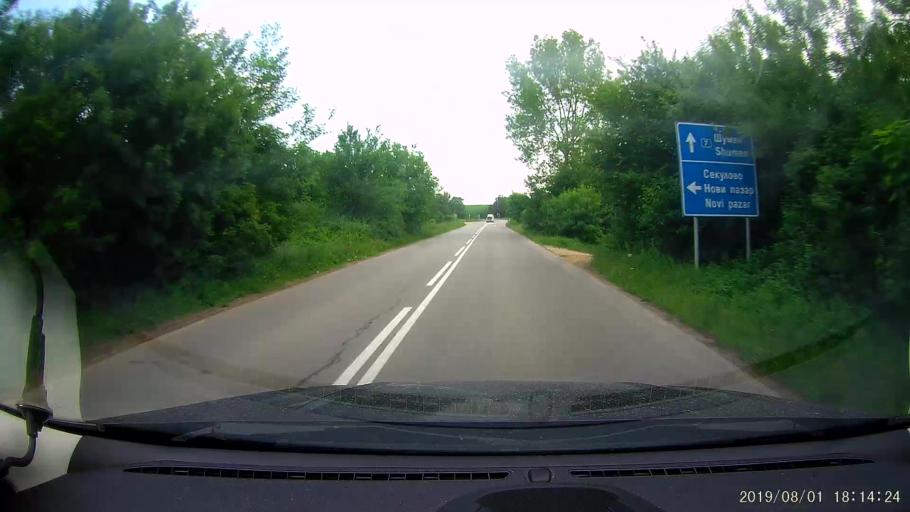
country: BG
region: Silistra
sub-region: Obshtina Dulovo
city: Dulovo
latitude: 43.7698
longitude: 27.1257
